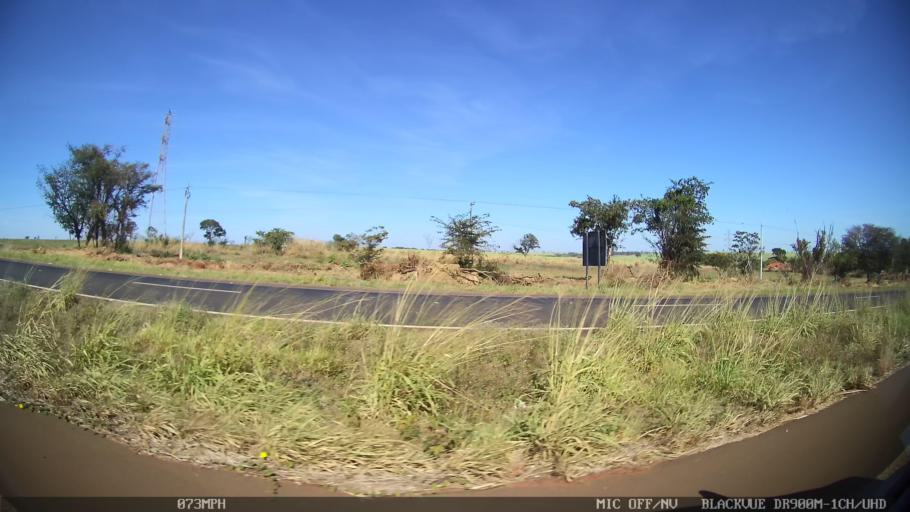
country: BR
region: Sao Paulo
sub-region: Barretos
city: Barretos
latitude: -20.5455
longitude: -48.6241
